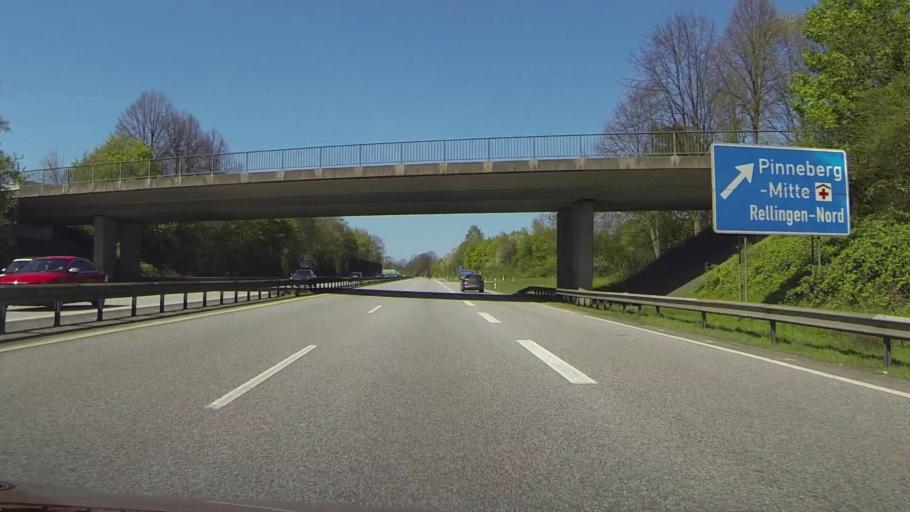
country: DE
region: Schleswig-Holstein
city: Rellingen
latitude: 53.6545
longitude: 9.8213
